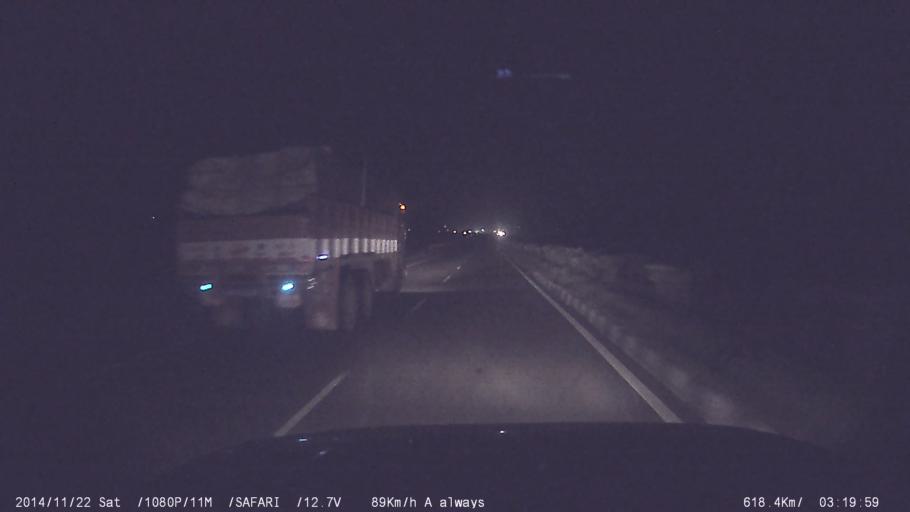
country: IN
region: Tamil Nadu
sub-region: Salem
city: Attayyampatti
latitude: 11.5734
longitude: 78.0383
